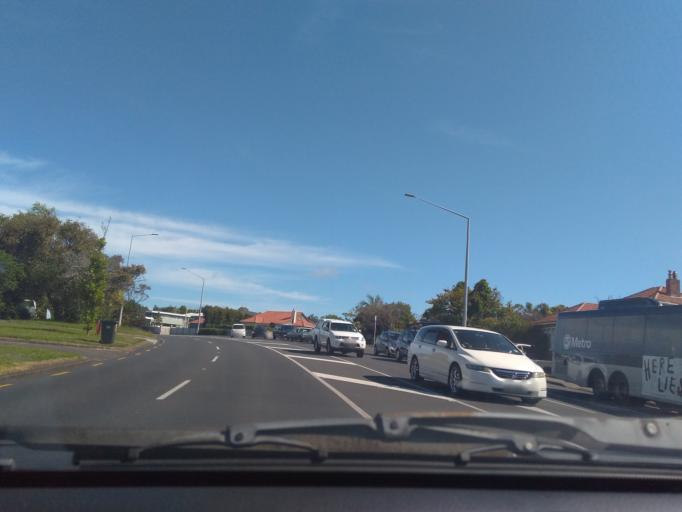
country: NZ
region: Auckland
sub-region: Auckland
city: Waitakere
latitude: -36.8944
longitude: 174.6450
